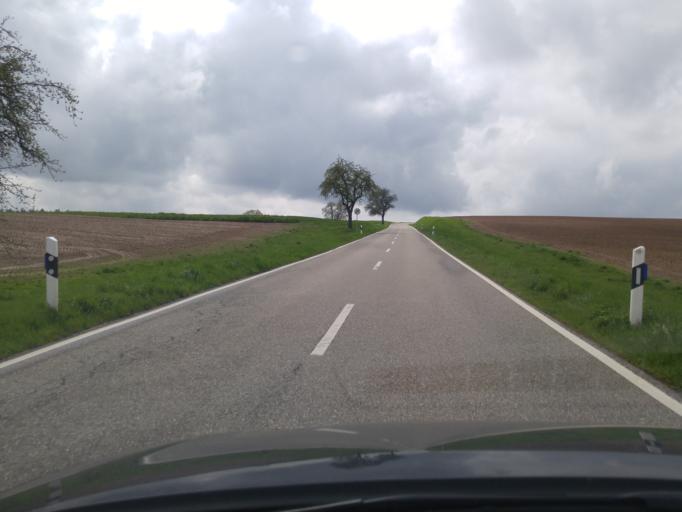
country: DE
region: Baden-Wuerttemberg
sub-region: Karlsruhe Region
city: Reichartshausen
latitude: 49.3300
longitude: 8.9522
